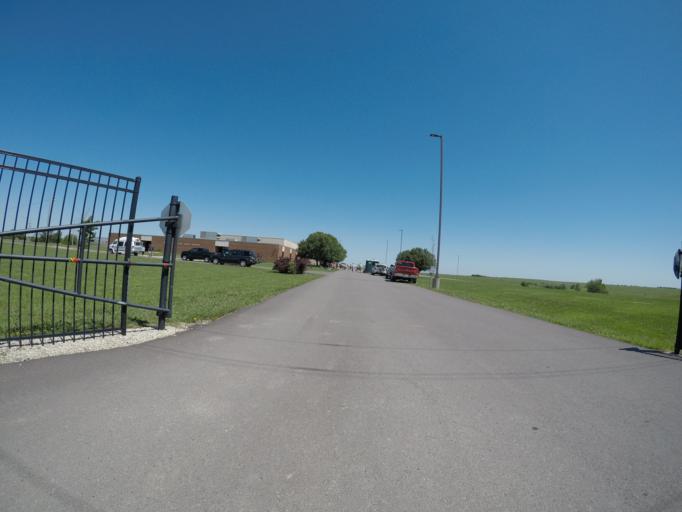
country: US
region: Kansas
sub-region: Shawnee County
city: Auburn
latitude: 38.8849
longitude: -96.0012
